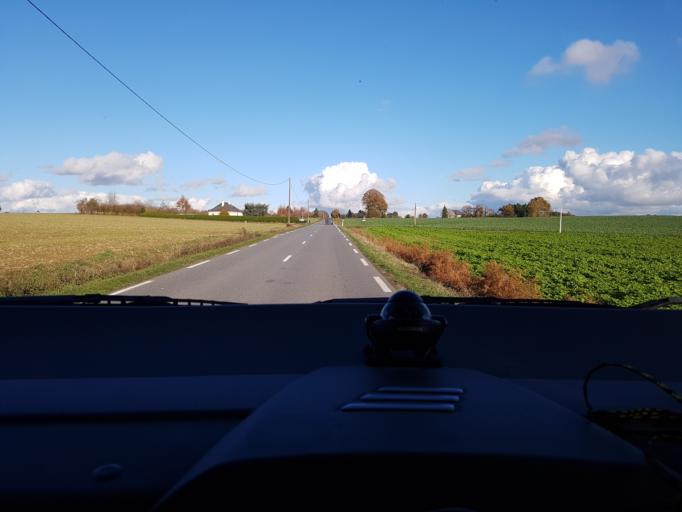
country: FR
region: Brittany
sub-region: Departement d'Ille-et-Vilaine
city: Pire-sur-Seiche
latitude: 48.0158
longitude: -1.4148
